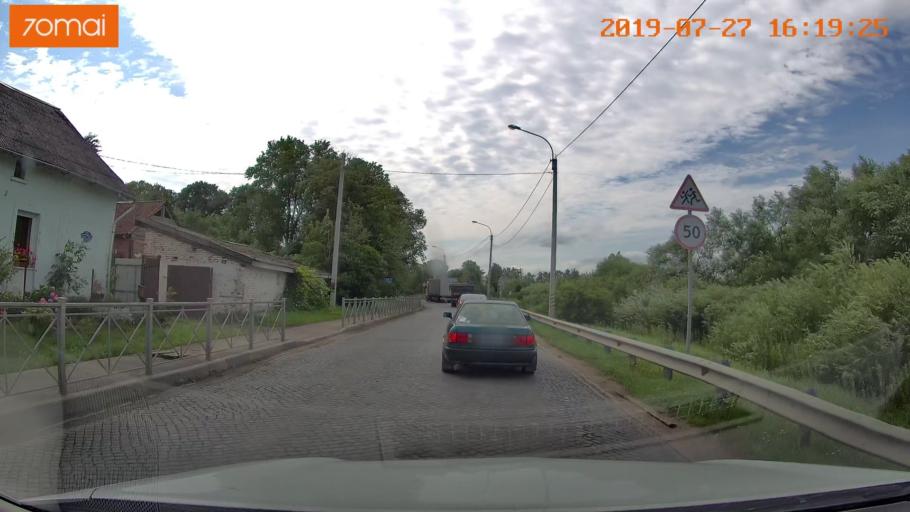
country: RU
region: Kaliningrad
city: Chernyakhovsk
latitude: 54.6257
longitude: 21.5315
